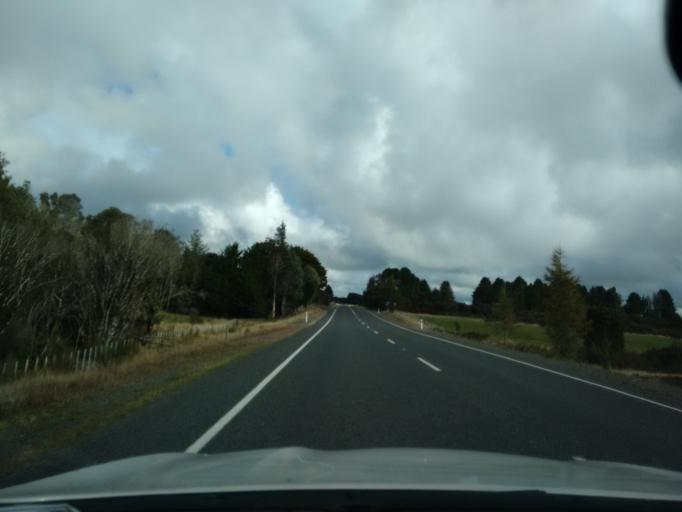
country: NZ
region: Manawatu-Wanganui
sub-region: Ruapehu District
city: Waiouru
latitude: -39.2890
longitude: 175.3872
